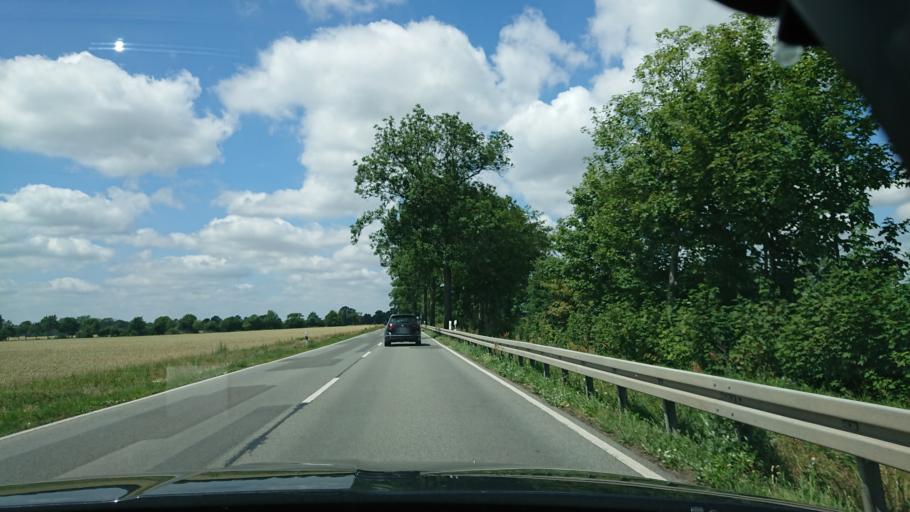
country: DE
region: Brandenburg
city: Perleberg
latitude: 53.0545
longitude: 11.9154
